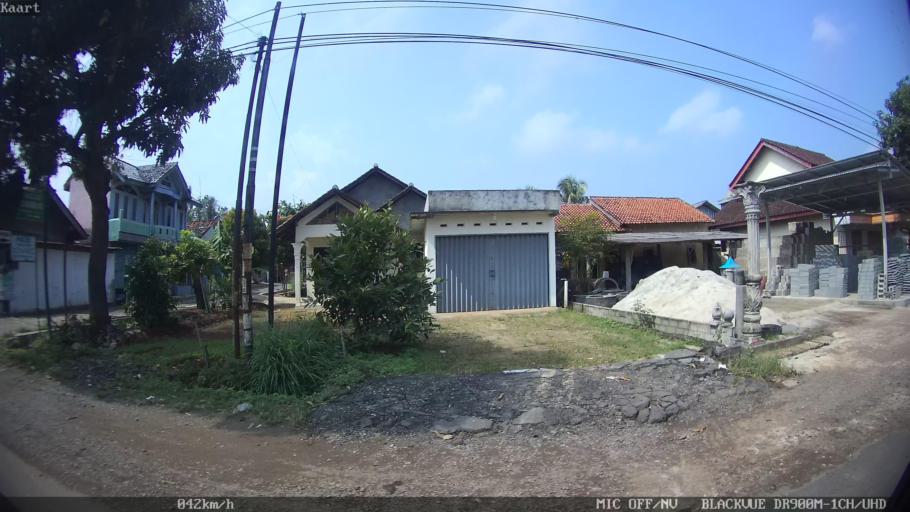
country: ID
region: Lampung
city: Gedongtataan
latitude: -5.3742
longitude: 105.0821
